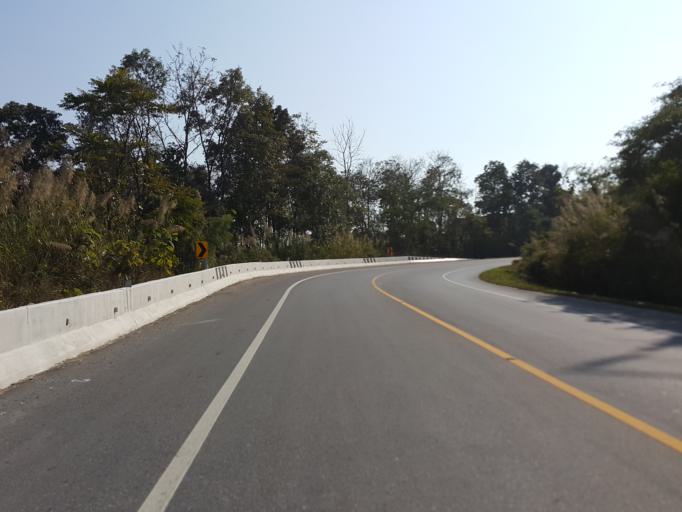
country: TH
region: Lampang
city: Chae Hom
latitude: 18.6022
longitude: 99.5475
